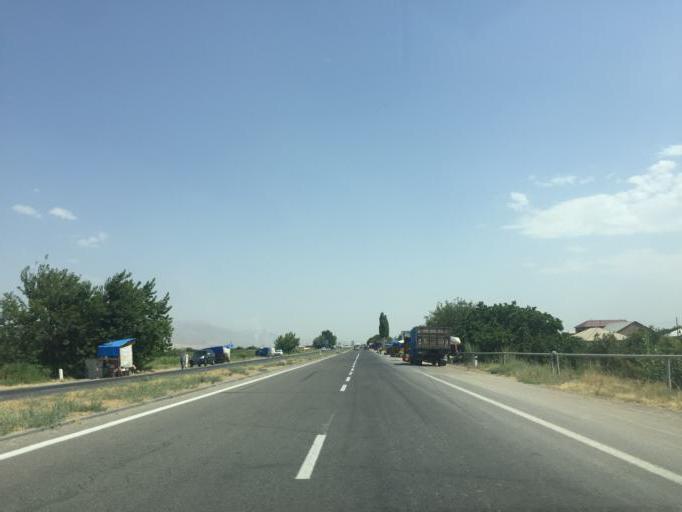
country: AM
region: Ararat
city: Shahumyan
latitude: 39.9096
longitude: 44.6031
